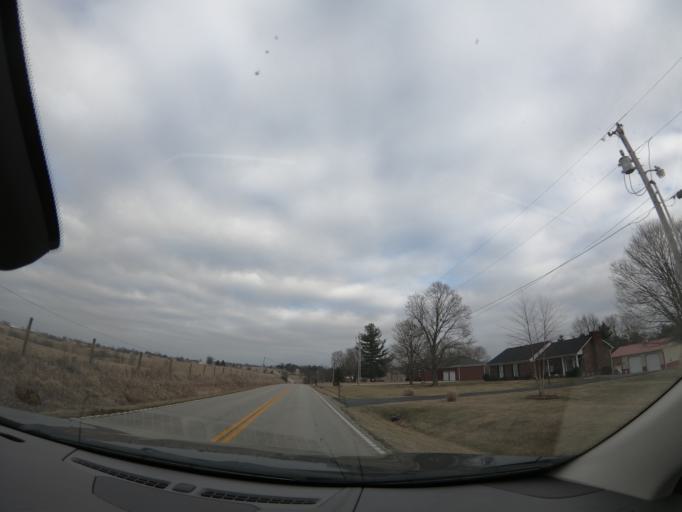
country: US
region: Kentucky
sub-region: Nelson County
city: Bardstown
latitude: 37.8509
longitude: -85.3537
